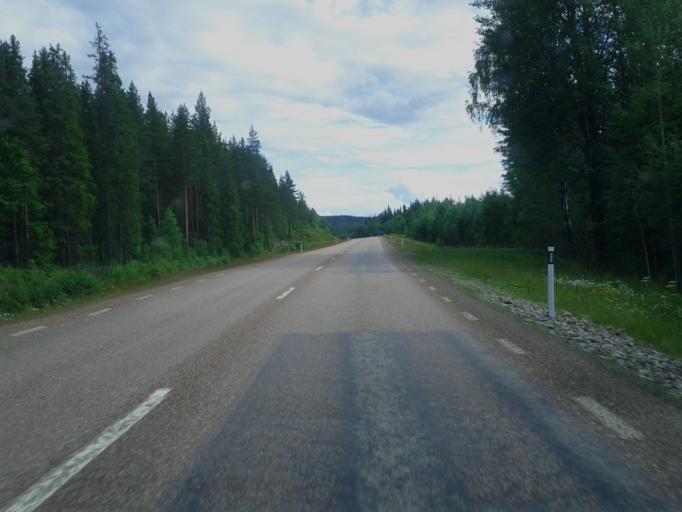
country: SE
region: Dalarna
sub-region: Rattviks Kommun
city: Raettvik
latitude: 60.7985
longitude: 15.2704
